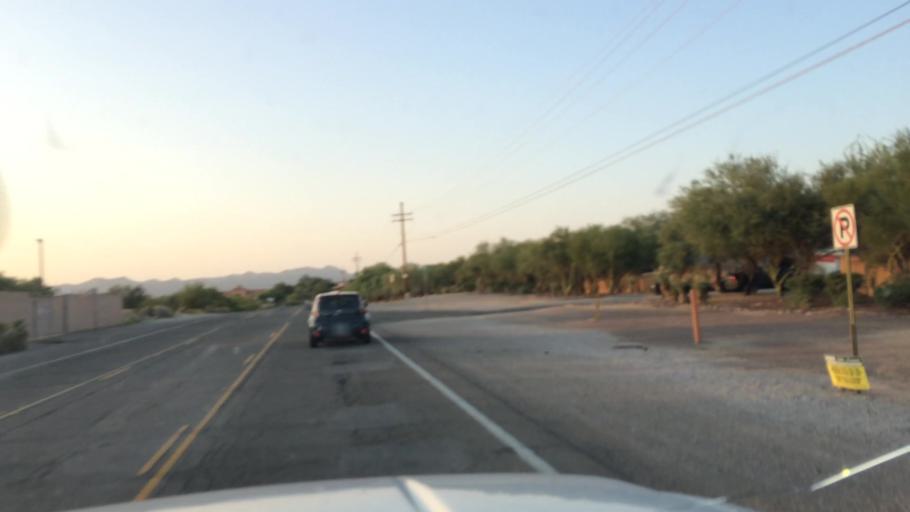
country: US
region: Arizona
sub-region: Pima County
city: Casas Adobes
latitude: 32.3439
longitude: -111.0204
